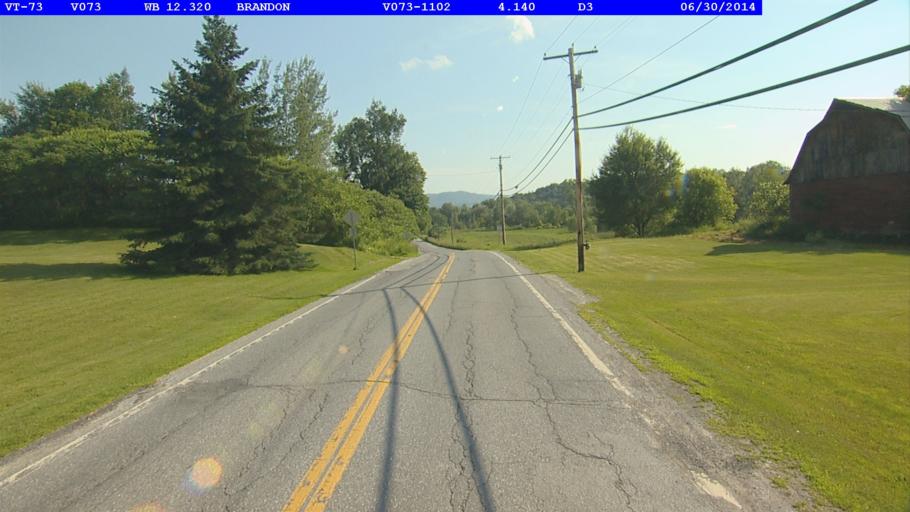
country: US
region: Vermont
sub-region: Rutland County
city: Brandon
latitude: 43.8092
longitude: -73.0766
